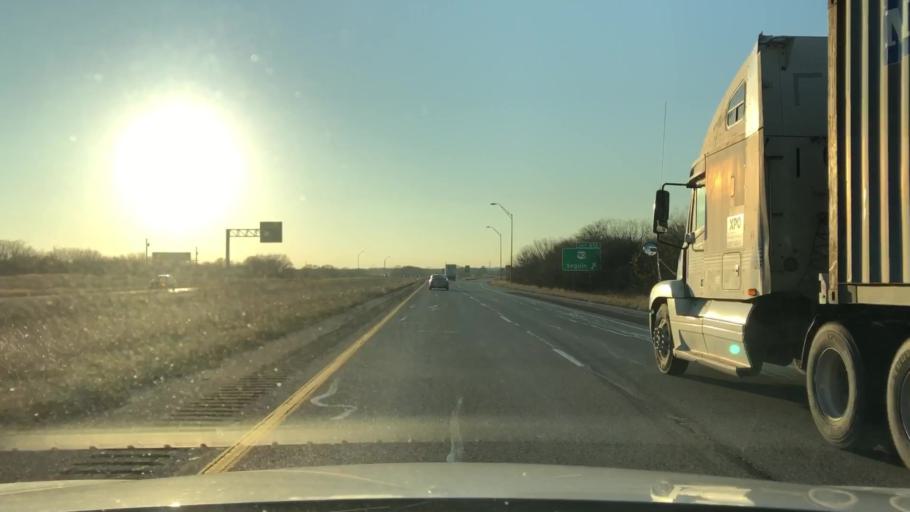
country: US
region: Texas
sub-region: Guadalupe County
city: Seguin
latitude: 29.6020
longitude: -97.9071
